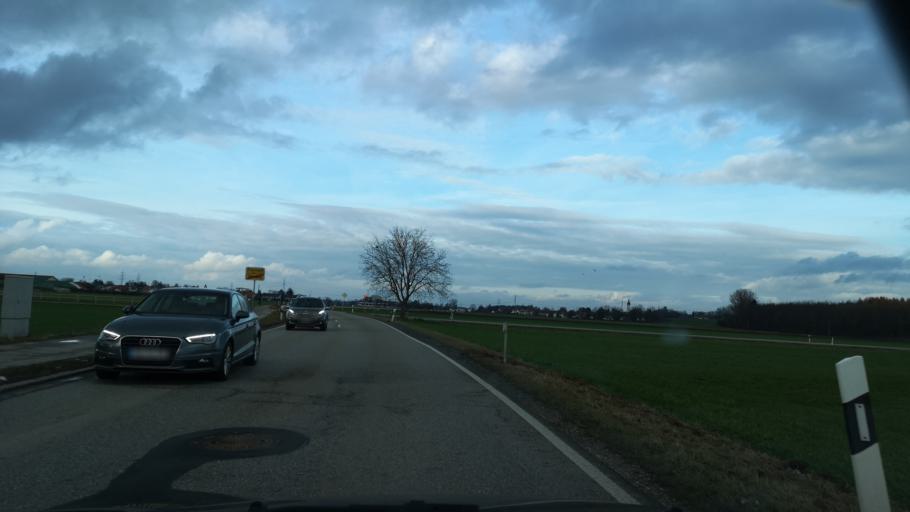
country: DE
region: Bavaria
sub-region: Upper Bavaria
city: Pliening
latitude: 48.1849
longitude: 11.8078
